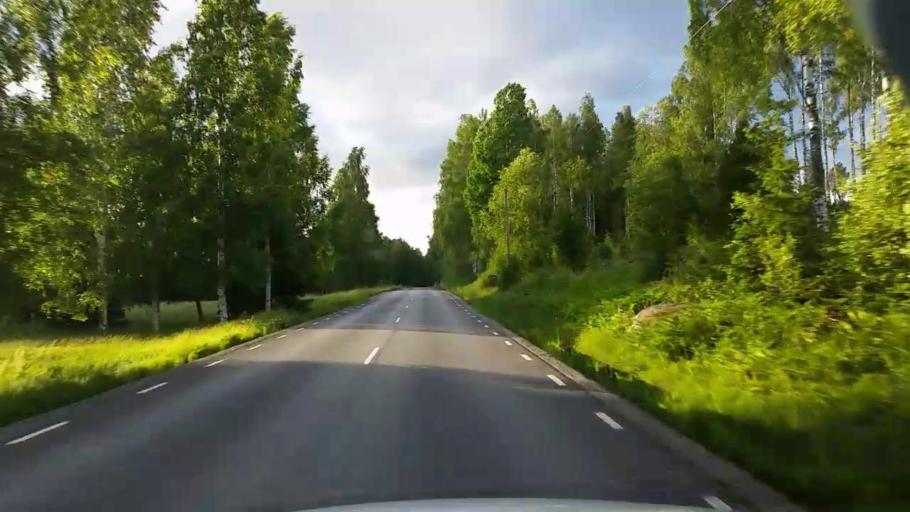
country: SE
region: Vaestmanland
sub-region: Kopings Kommun
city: Kolsva
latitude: 59.7344
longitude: 15.8257
